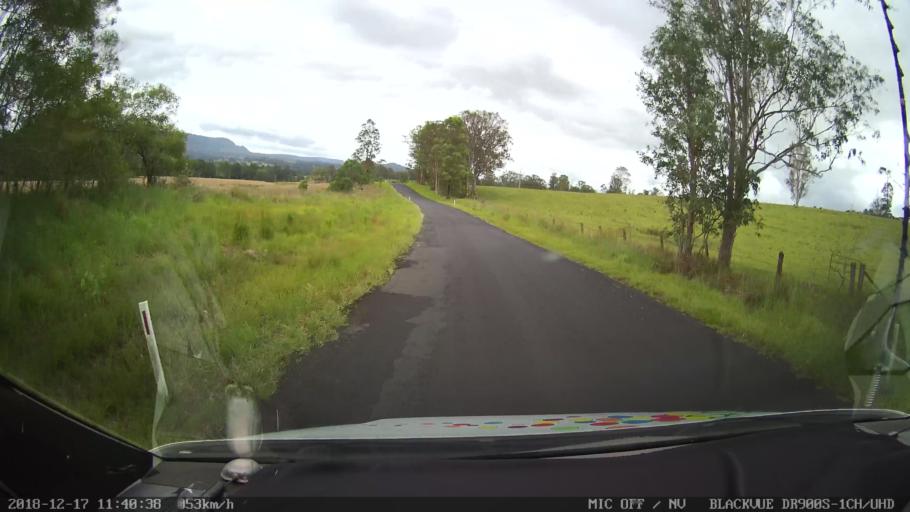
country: AU
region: New South Wales
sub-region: Kyogle
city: Kyogle
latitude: -28.6806
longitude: 152.5930
